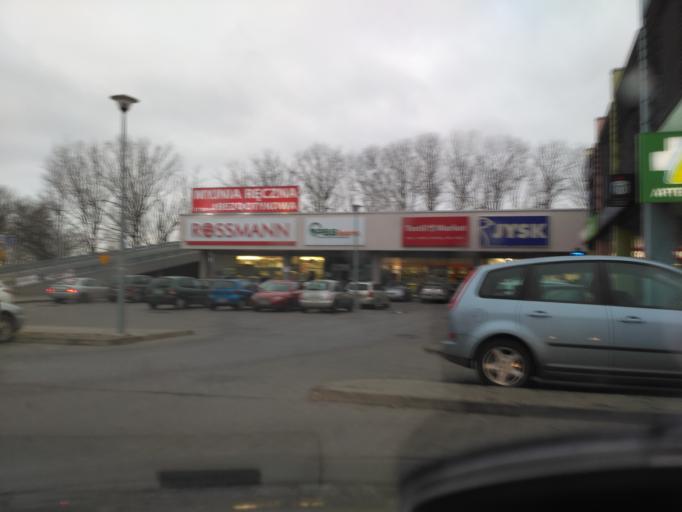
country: PL
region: Lublin Voivodeship
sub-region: Powiat lubelski
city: Lublin
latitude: 51.2680
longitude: 22.5414
